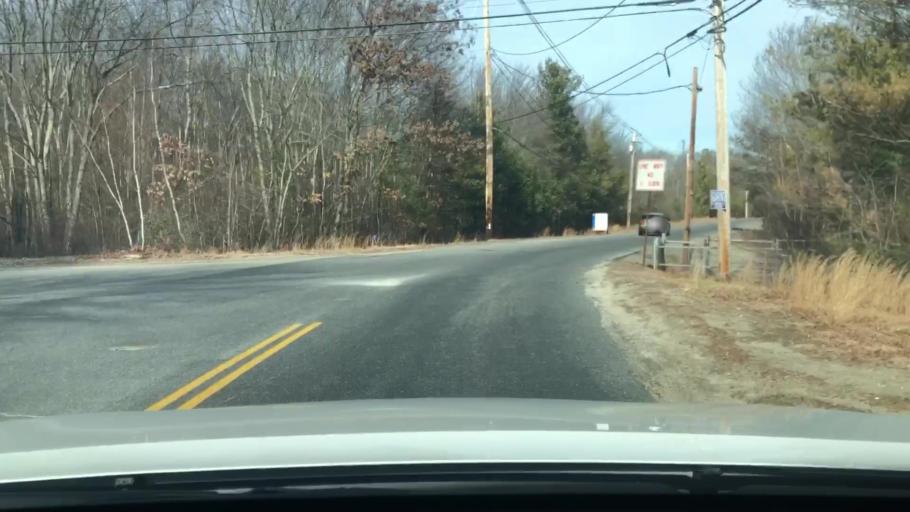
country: US
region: Massachusetts
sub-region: Worcester County
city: Milford
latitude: 42.1426
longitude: -71.4880
